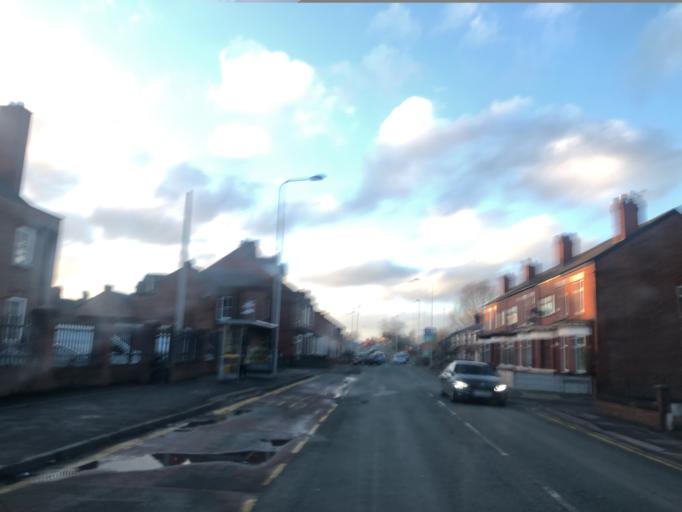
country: GB
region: England
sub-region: Cheshire West and Chester
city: Marston
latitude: 53.2599
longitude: -2.4948
